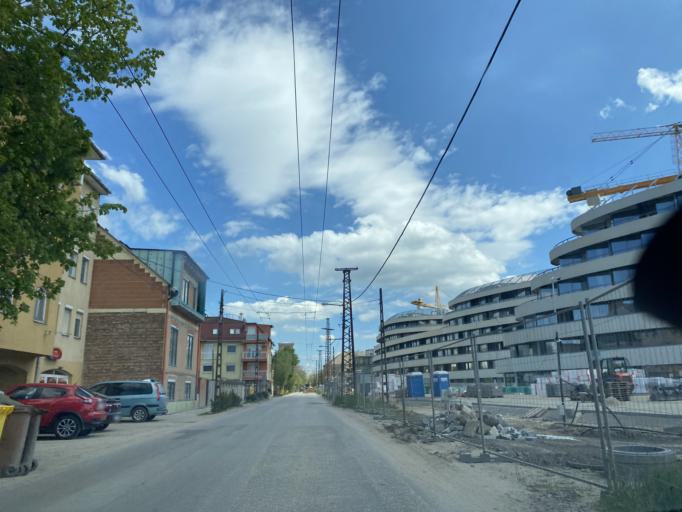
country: HU
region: Csongrad
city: Szeged
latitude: 46.2577
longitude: 20.1313
